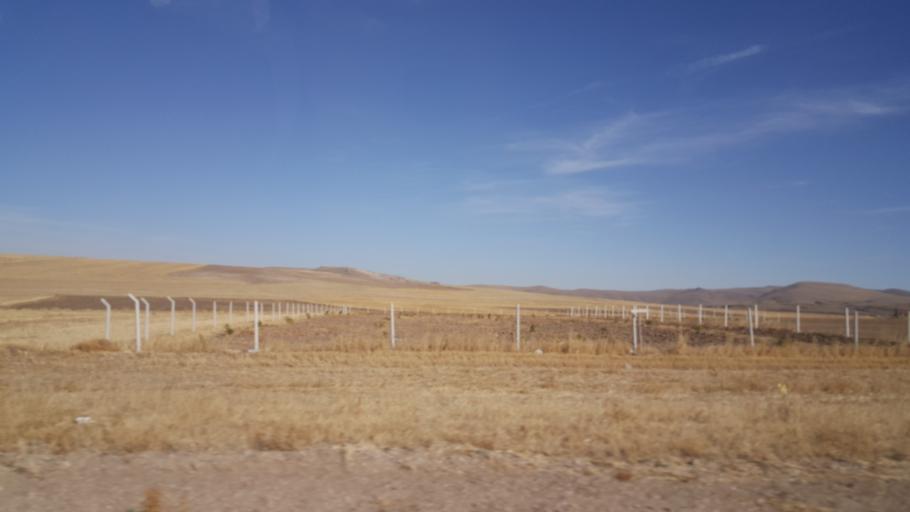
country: TR
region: Ankara
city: Yenice
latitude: 39.3149
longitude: 32.7570
